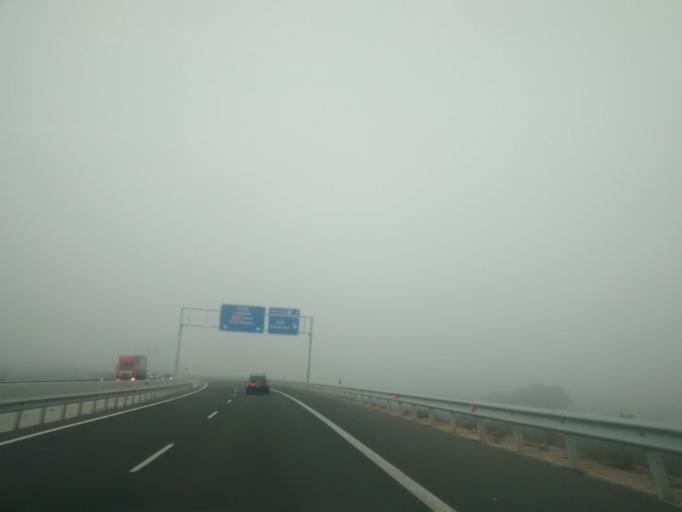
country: ES
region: Navarre
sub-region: Provincia de Navarra
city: Viana
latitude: 42.4563
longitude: -2.3615
